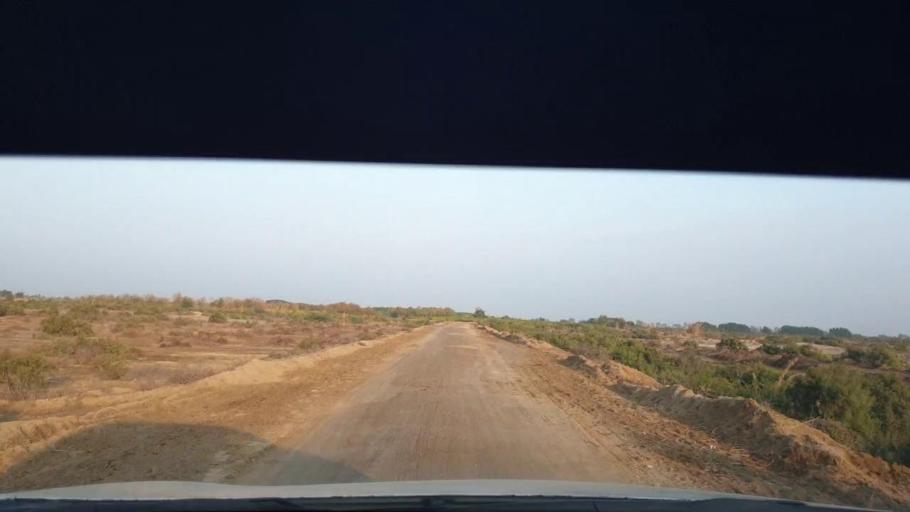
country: PK
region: Sindh
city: Berani
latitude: 25.7498
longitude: 68.9797
